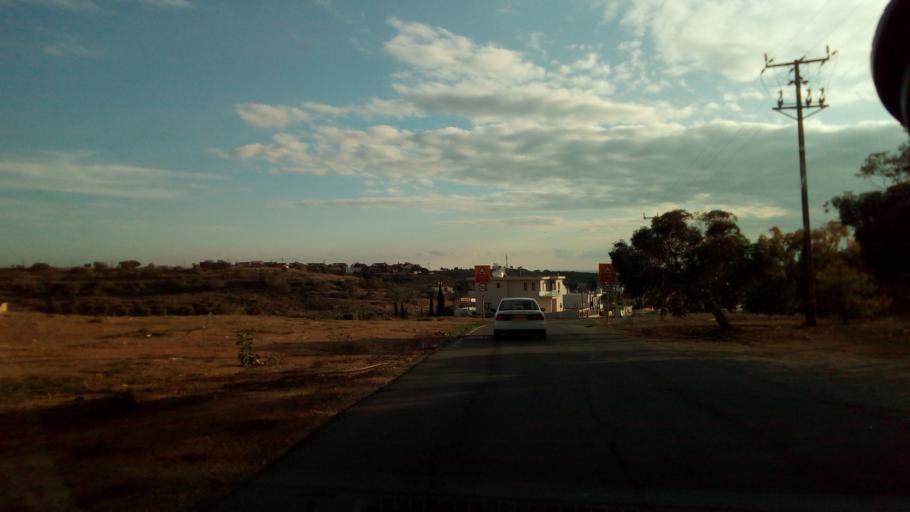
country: CY
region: Larnaka
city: Xylotymbou
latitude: 34.9980
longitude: 33.7837
